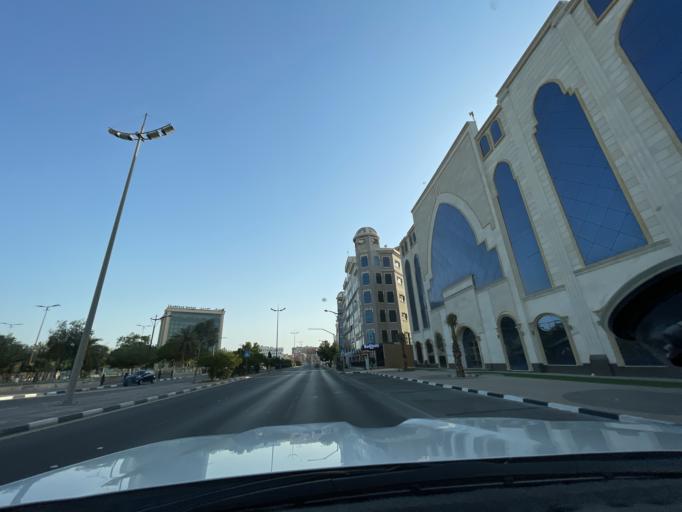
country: SA
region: Eastern Province
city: Khobar
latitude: 26.2844
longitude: 50.2047
